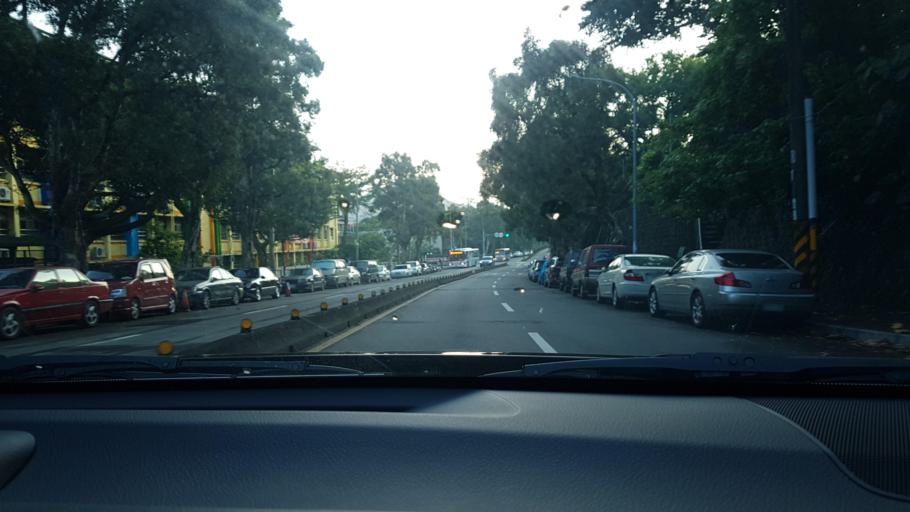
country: TW
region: Taipei
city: Taipei
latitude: 25.1045
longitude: 121.5565
